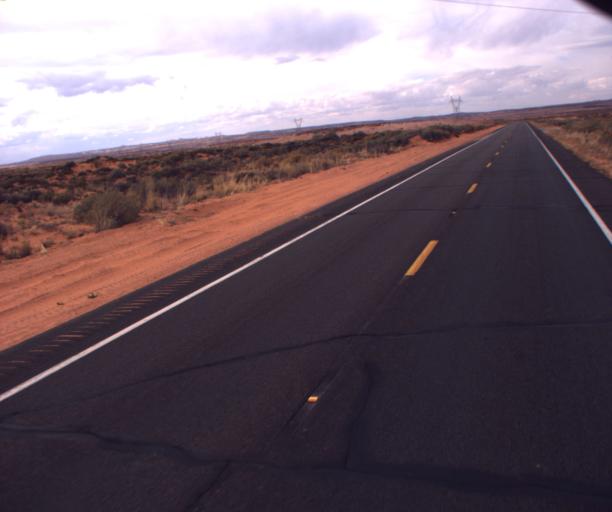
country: US
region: Arizona
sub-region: Apache County
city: Many Farms
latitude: 36.9366
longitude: -109.6351
